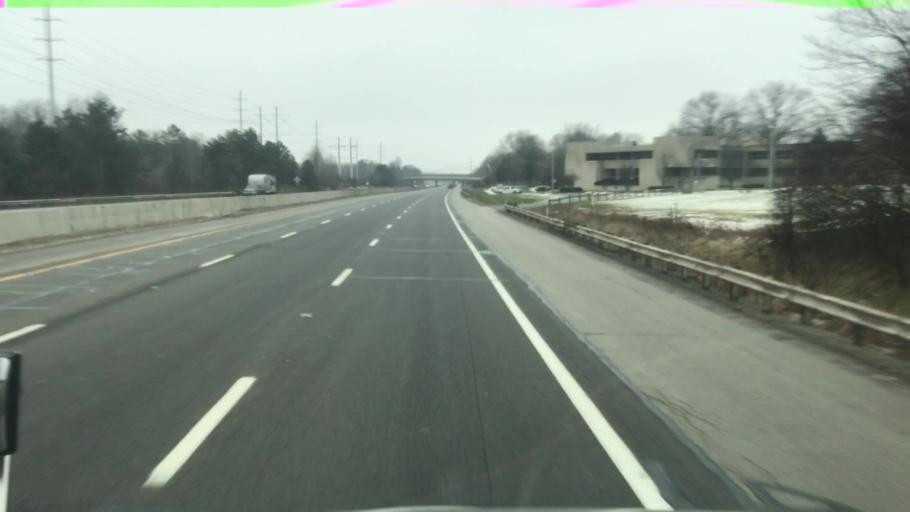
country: US
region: Ohio
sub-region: Cuyahoga County
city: Berea
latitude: 41.3479
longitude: -81.8593
